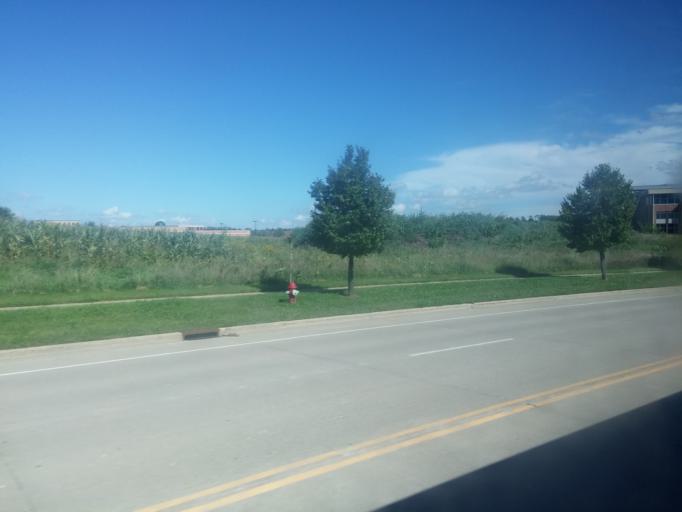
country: US
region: Wisconsin
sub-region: Dane County
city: Windsor
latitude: 43.1458
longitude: -89.2973
